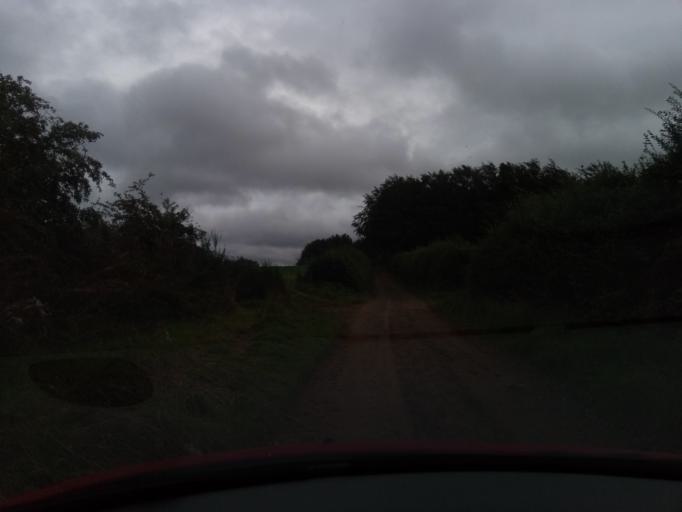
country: GB
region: Scotland
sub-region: The Scottish Borders
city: Jedburgh
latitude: 55.4875
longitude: -2.5197
